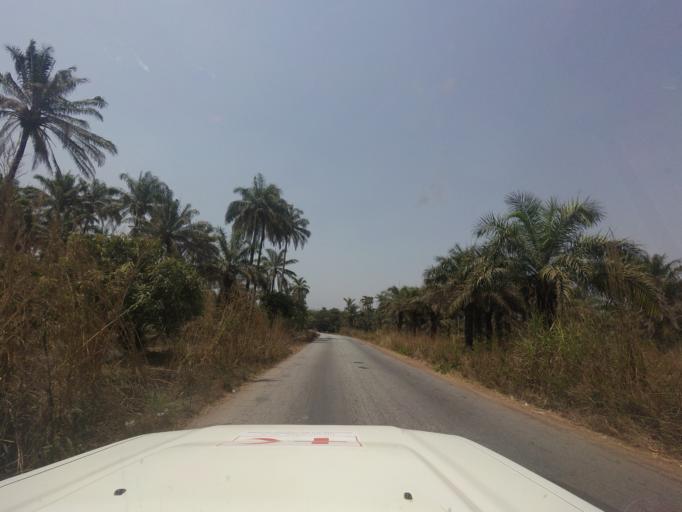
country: GN
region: Kindia
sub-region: Kindia
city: Kindia
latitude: 9.9466
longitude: -12.9593
